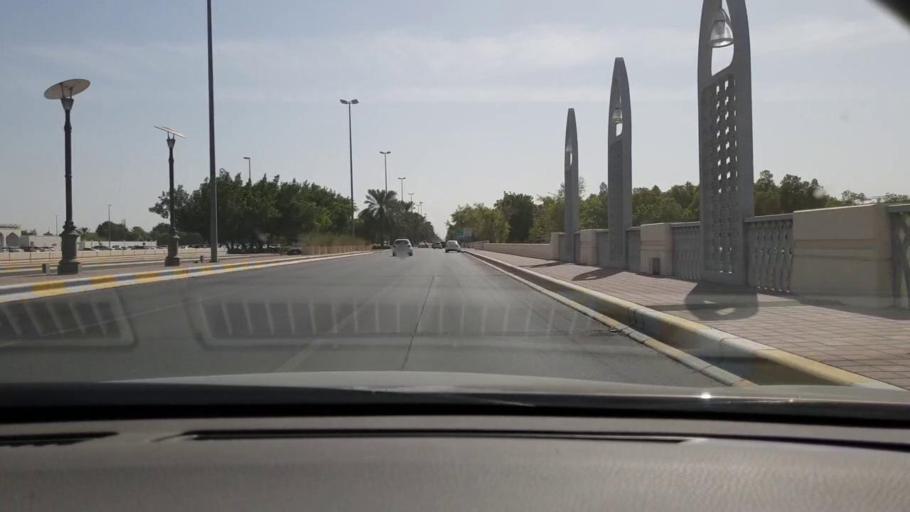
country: AE
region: Abu Dhabi
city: Al Ain
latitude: 24.2352
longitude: 55.7386
